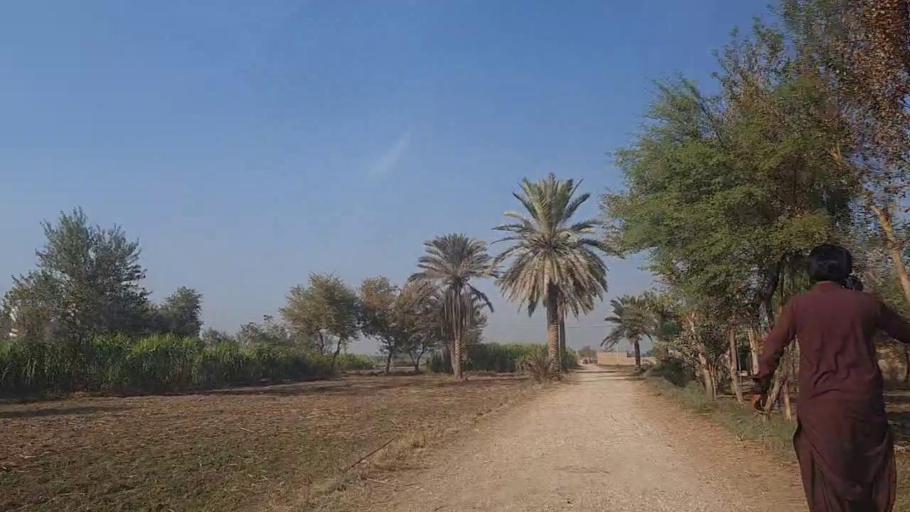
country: PK
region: Sindh
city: Gambat
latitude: 27.3710
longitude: 68.4745
